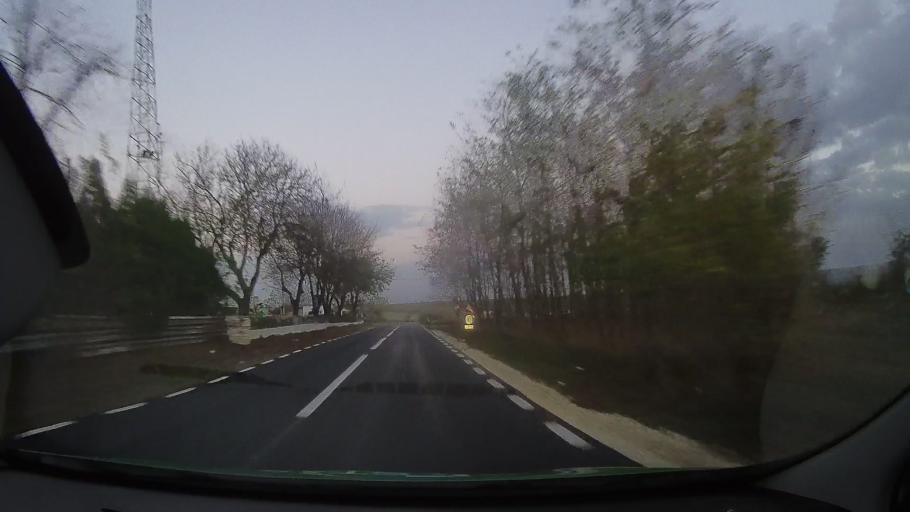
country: RO
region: Constanta
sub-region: Comuna Baneasa
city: Baneasa
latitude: 44.0790
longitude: 27.6935
